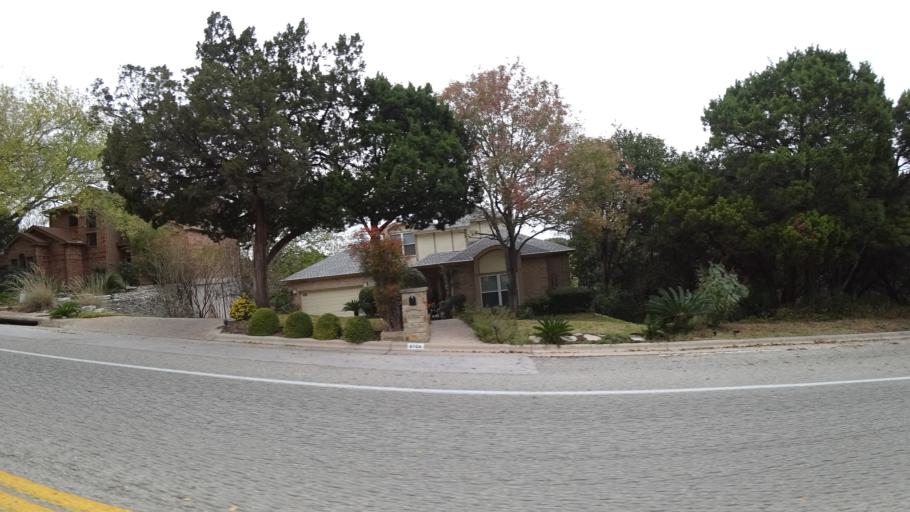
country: US
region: Texas
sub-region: Williamson County
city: Jollyville
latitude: 30.3775
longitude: -97.7918
